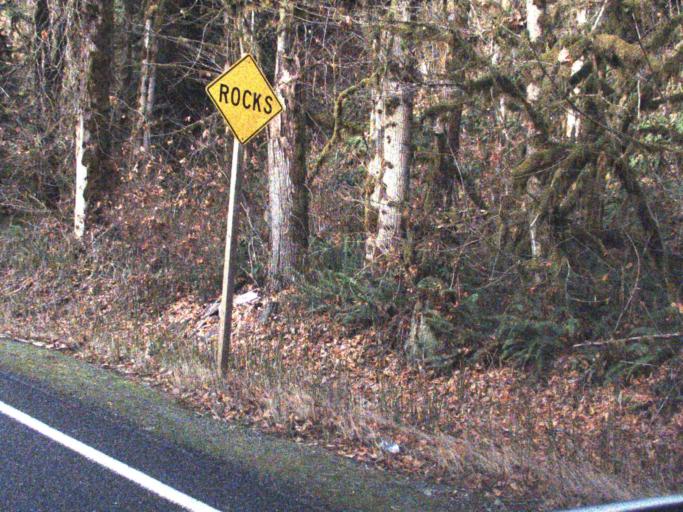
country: US
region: Washington
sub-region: Snohomish County
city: Darrington
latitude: 48.3767
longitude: -121.5490
